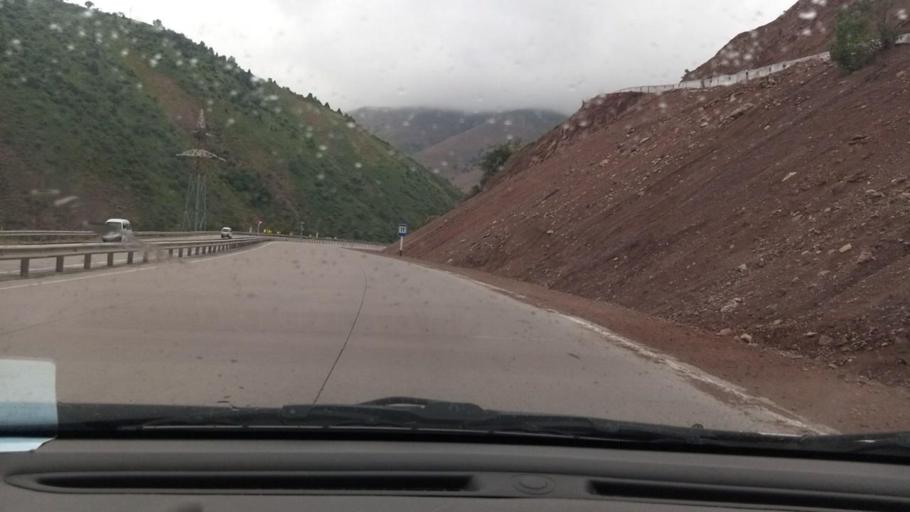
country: UZ
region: Toshkent
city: Angren
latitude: 41.1444
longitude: 70.4484
